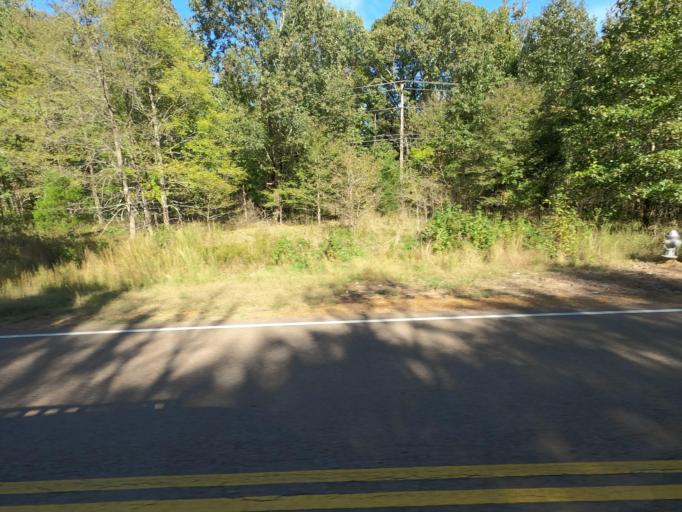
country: US
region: Tennessee
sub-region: Shelby County
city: Arlington
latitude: 35.2522
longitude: -89.6538
